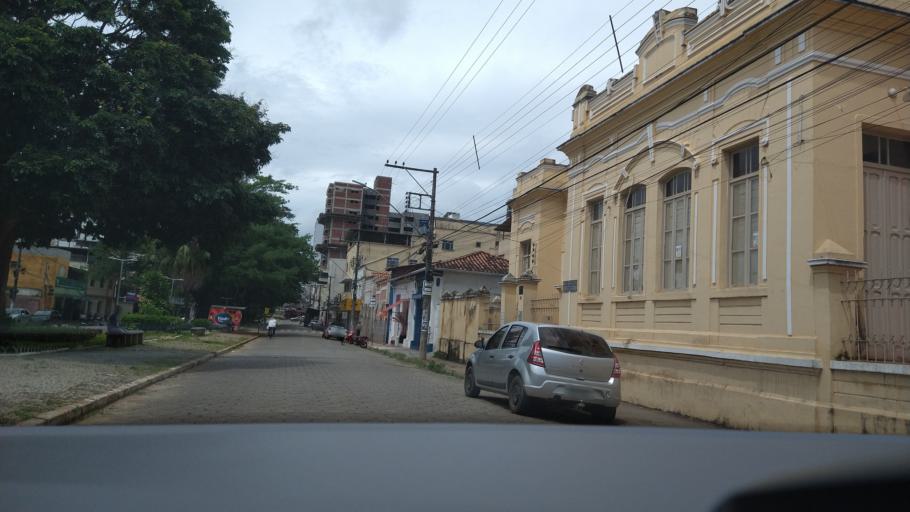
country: BR
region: Minas Gerais
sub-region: Vicosa
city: Vicosa
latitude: -20.7594
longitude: -42.8796
